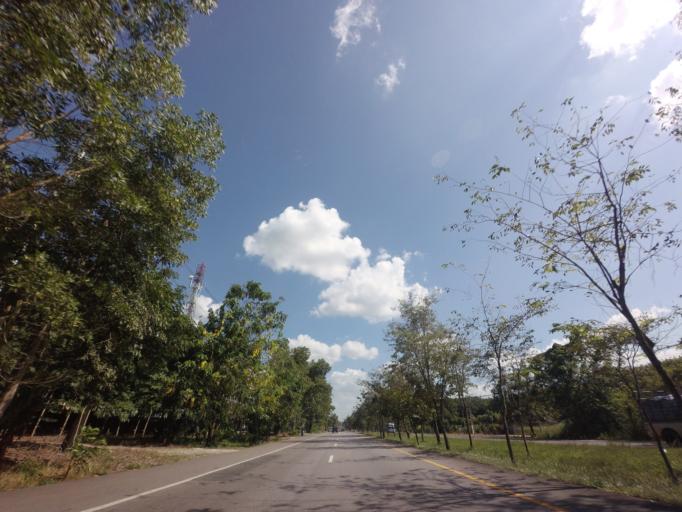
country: TH
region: Rayong
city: Wang Chan
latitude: 12.9556
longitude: 101.5080
